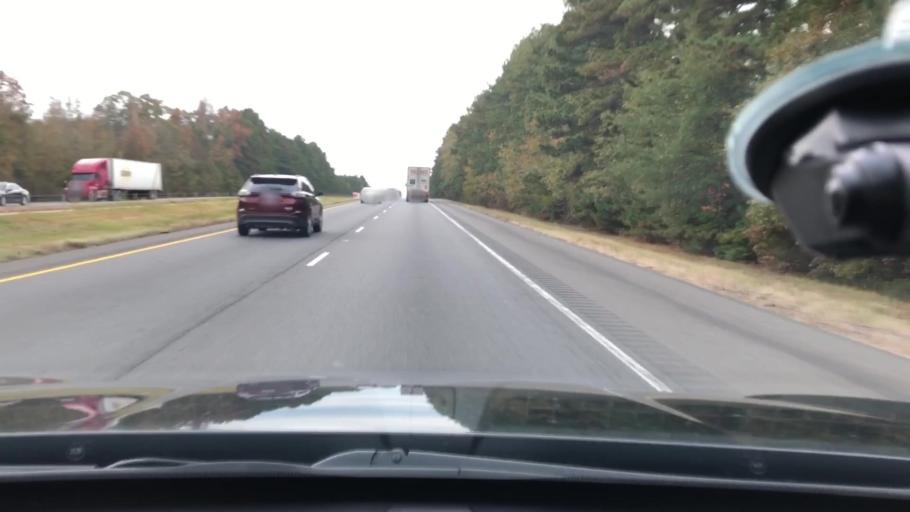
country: US
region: Arkansas
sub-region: Clark County
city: Arkadelphia
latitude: 34.0571
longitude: -93.1301
